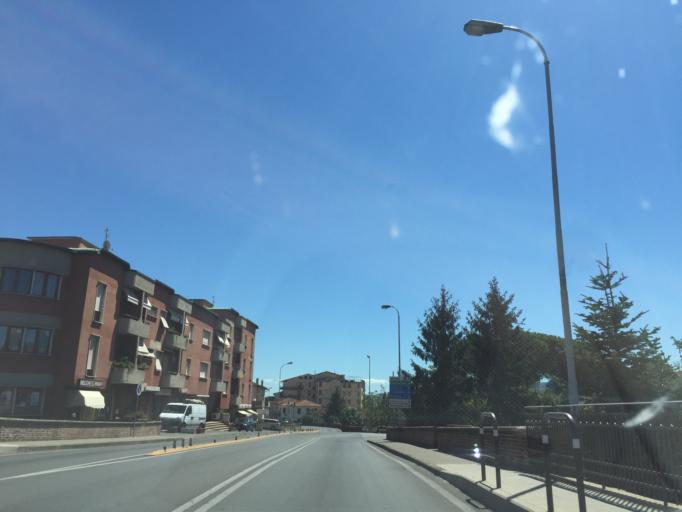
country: IT
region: Tuscany
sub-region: Provincia di Pistoia
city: Pistoia
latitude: 43.9272
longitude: 10.9191
